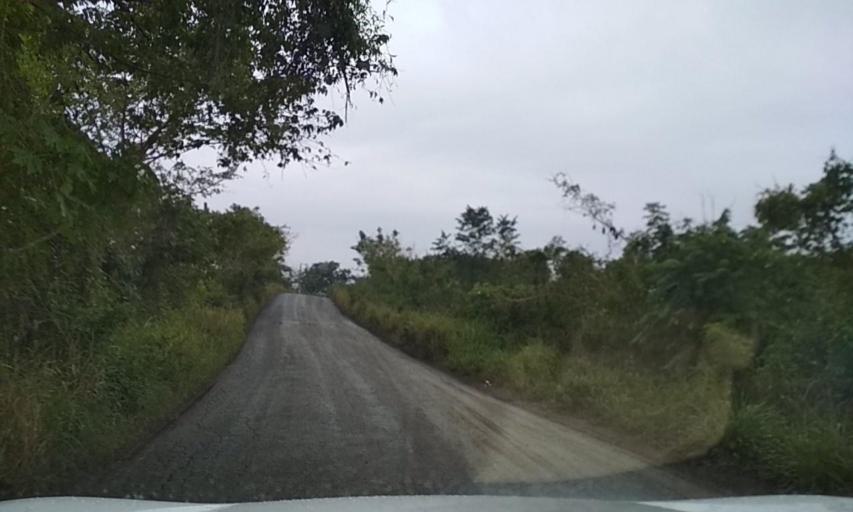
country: MX
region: Veracruz
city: Coatzintla
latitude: 20.4656
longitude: -97.4710
